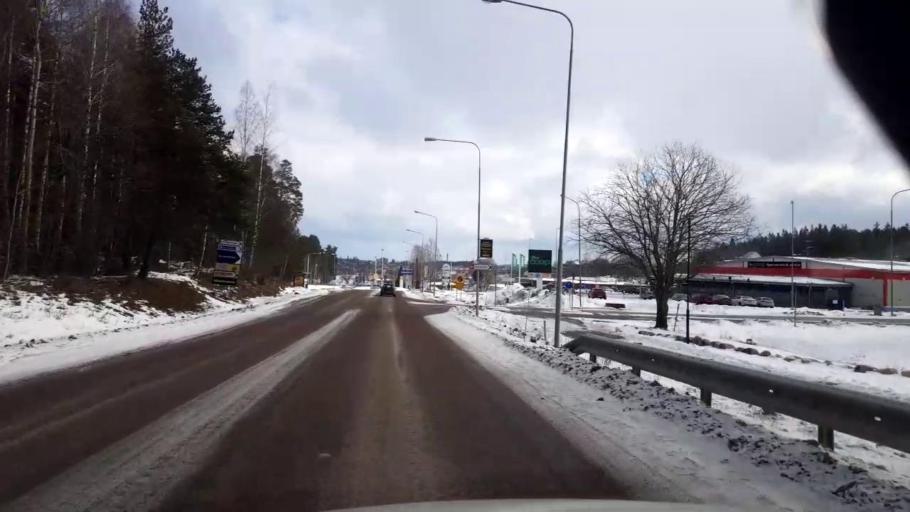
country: SE
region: Gaevleborg
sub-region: Hudiksvalls Kommun
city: Hudiksvall
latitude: 61.7363
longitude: 17.0918
